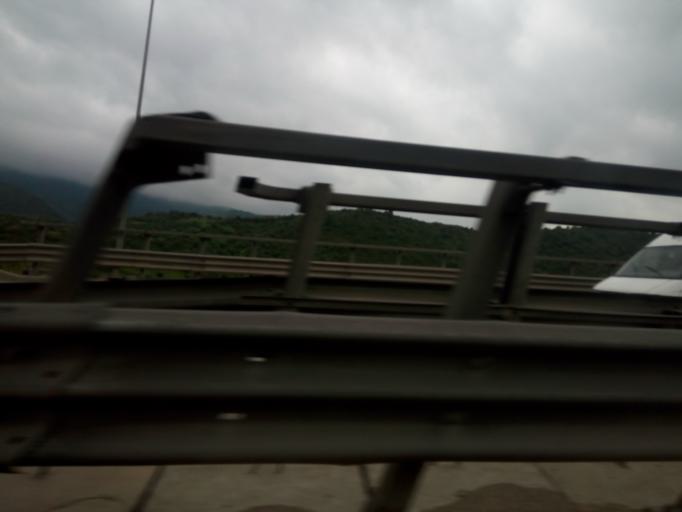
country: DZ
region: Bouira
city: Lakhdaria
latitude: 36.5773
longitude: 3.5525
